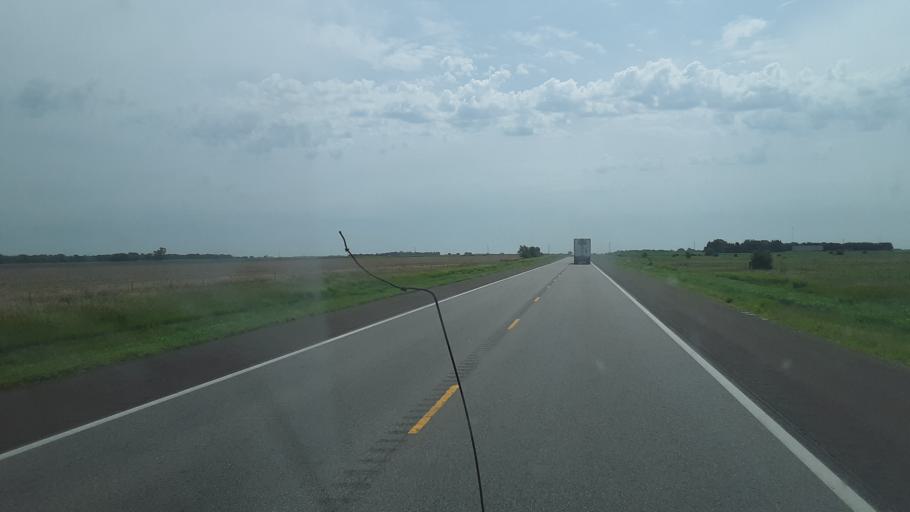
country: US
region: Kansas
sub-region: Reno County
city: Nickerson
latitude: 37.9849
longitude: -98.1144
